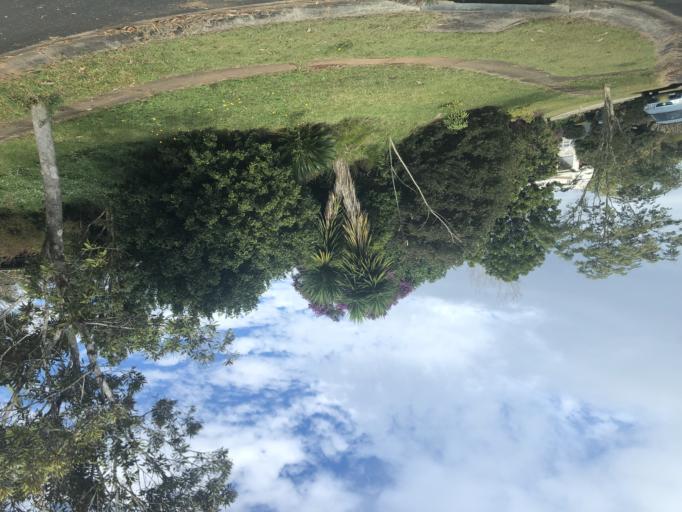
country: AU
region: New South Wales
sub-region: Bellingen
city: Bellingen
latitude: -30.4451
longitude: 152.9014
